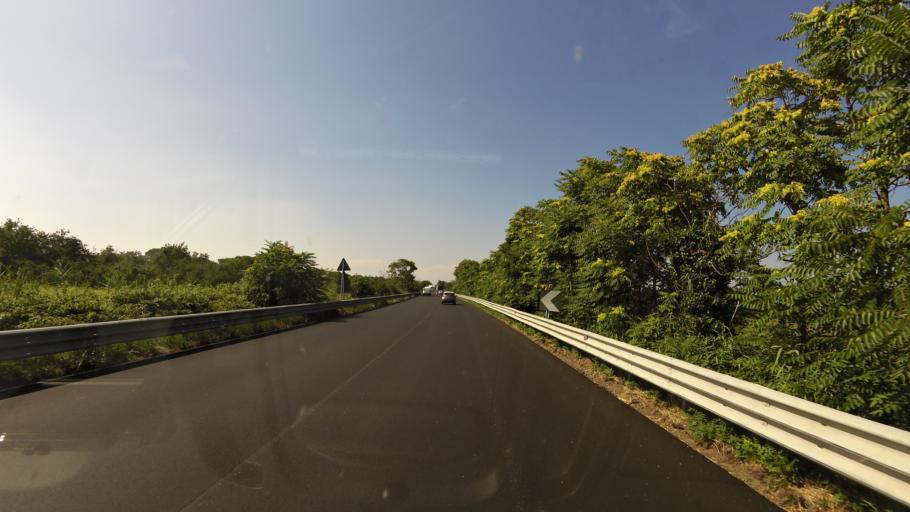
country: IT
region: Emilia-Romagna
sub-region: Provincia di Ravenna
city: Marina Romea
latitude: 44.5844
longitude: 12.2537
